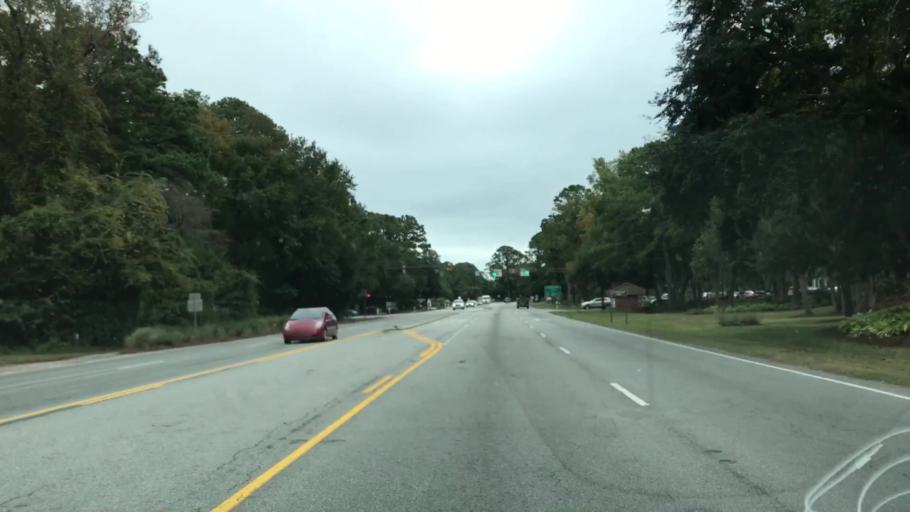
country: US
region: South Carolina
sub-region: Beaufort County
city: Hilton Head Island
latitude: 32.1587
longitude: -80.7653
